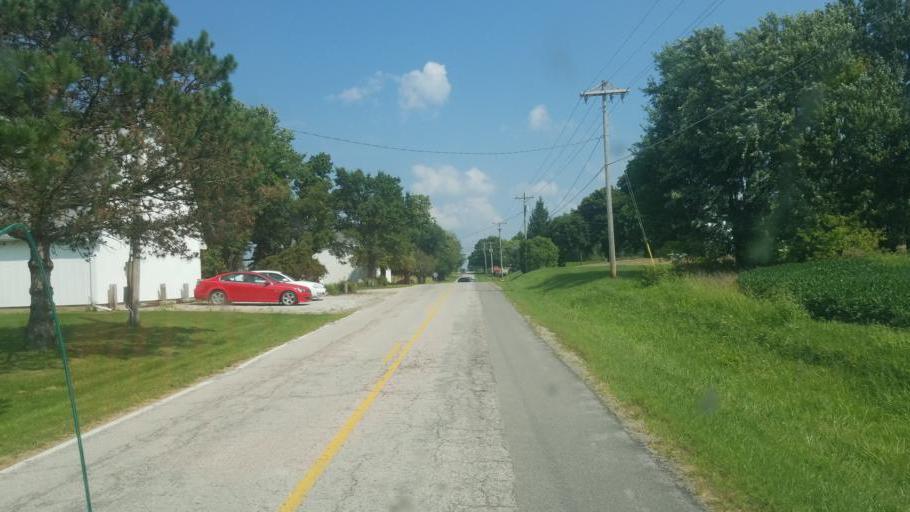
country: US
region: Ohio
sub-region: Huron County
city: New London
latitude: 41.0656
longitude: -82.3983
